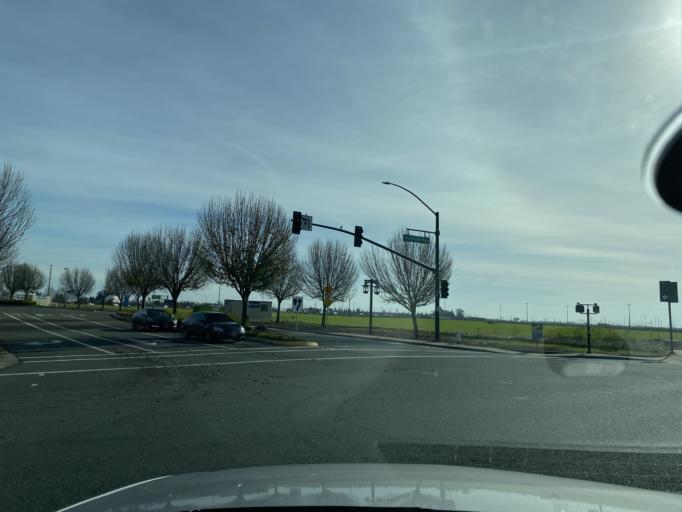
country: US
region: California
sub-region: Sacramento County
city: Elk Grove
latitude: 38.3839
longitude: -121.3728
